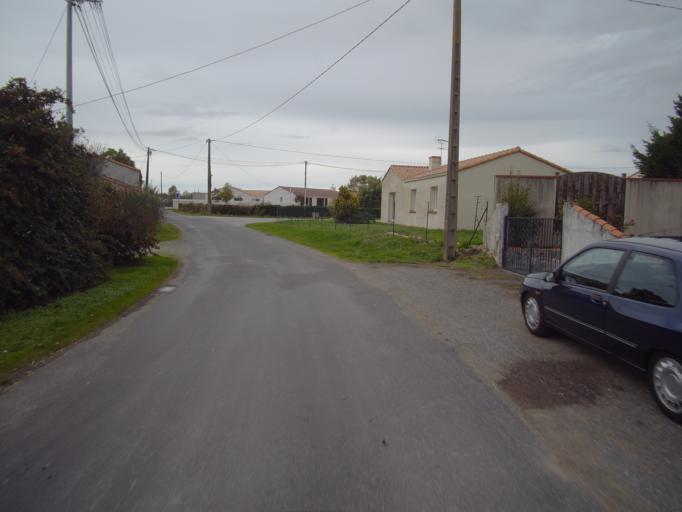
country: FR
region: Pays de la Loire
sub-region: Departement de la Loire-Atlantique
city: Remouille
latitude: 47.0309
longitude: -1.3894
